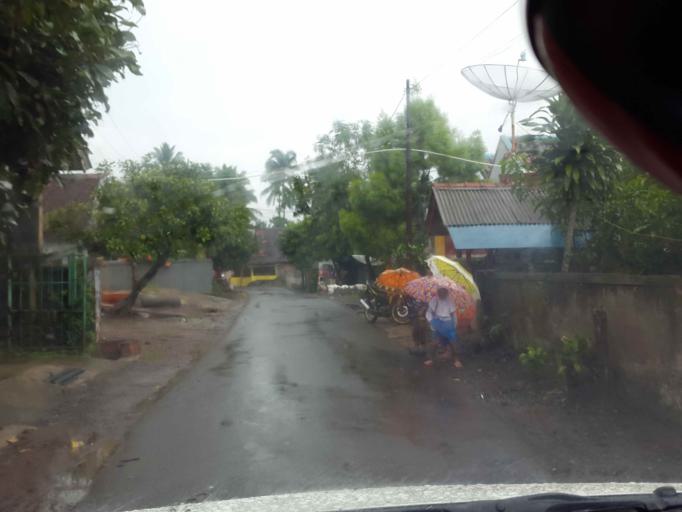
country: ID
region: West Java
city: Cilandak
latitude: -7.0010
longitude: 106.7171
